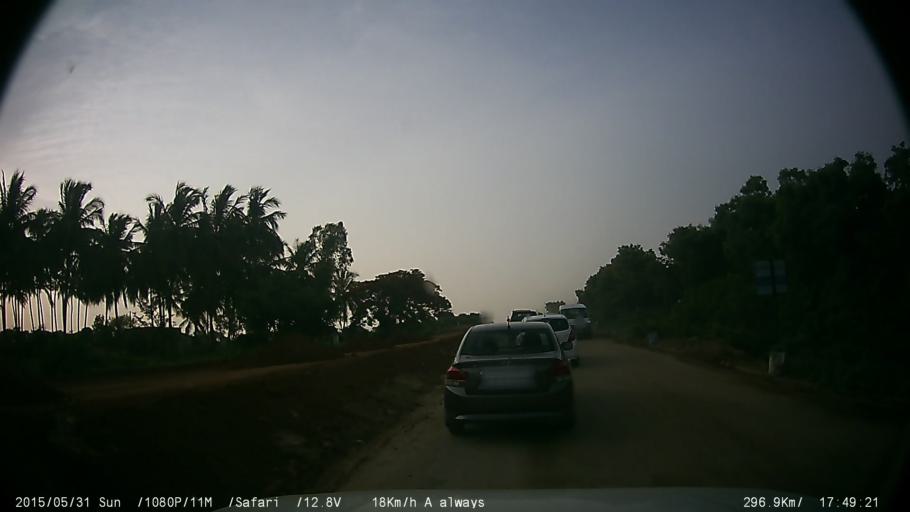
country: IN
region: Karnataka
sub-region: Mysore
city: Nanjangud
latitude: 11.9709
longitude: 76.6703
